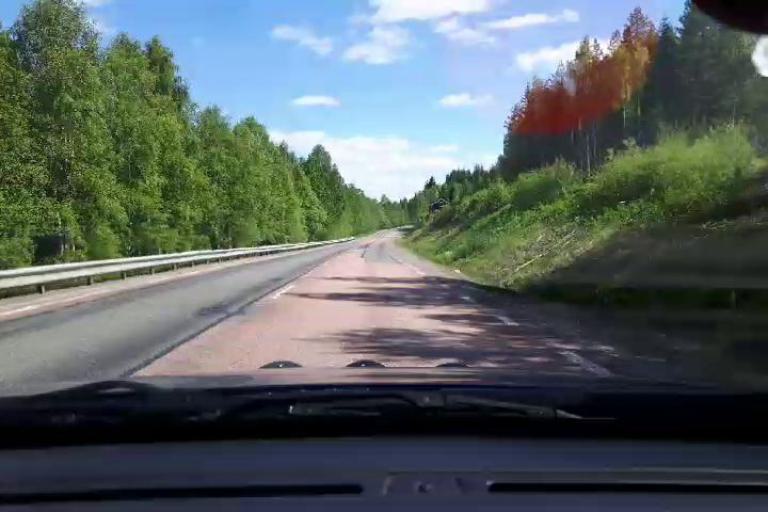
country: SE
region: Gaevleborg
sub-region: Ljusdals Kommun
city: Farila
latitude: 61.8869
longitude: 15.6954
